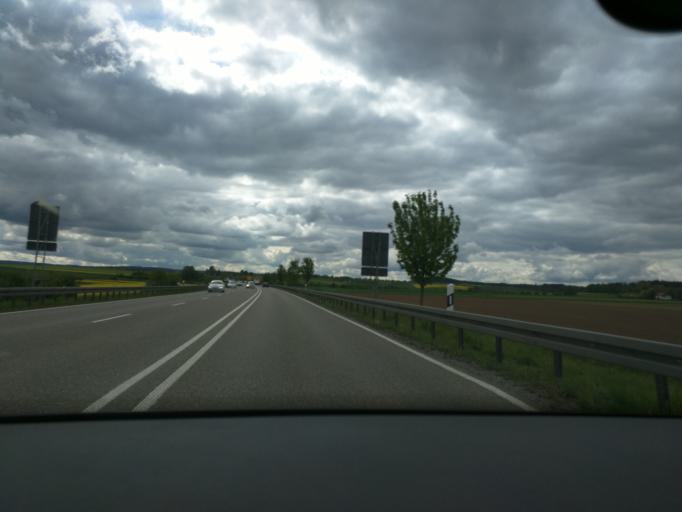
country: DE
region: Baden-Wuerttemberg
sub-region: Regierungsbezirk Stuttgart
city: Bondorf
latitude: 48.5072
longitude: 8.8119
